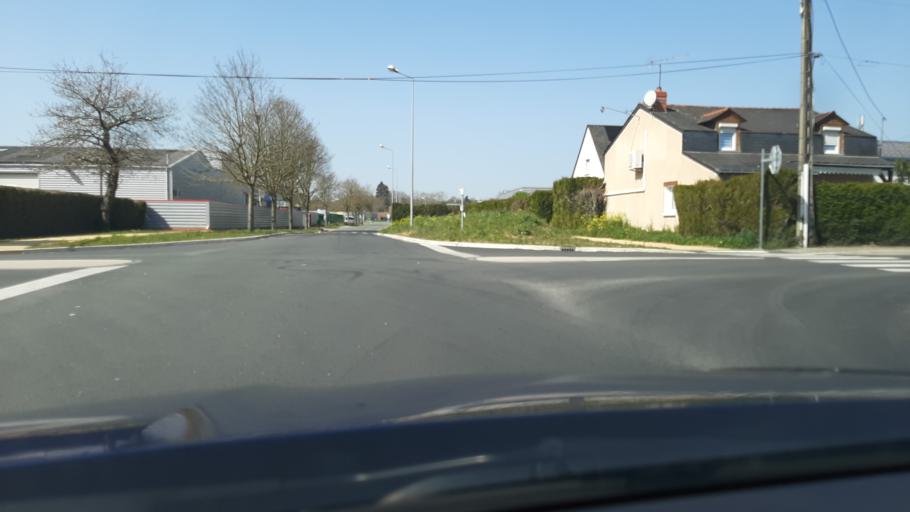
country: FR
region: Pays de la Loire
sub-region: Departement de Maine-et-Loire
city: Pellouailles-les-Vignes
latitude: 47.5196
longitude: -0.4359
